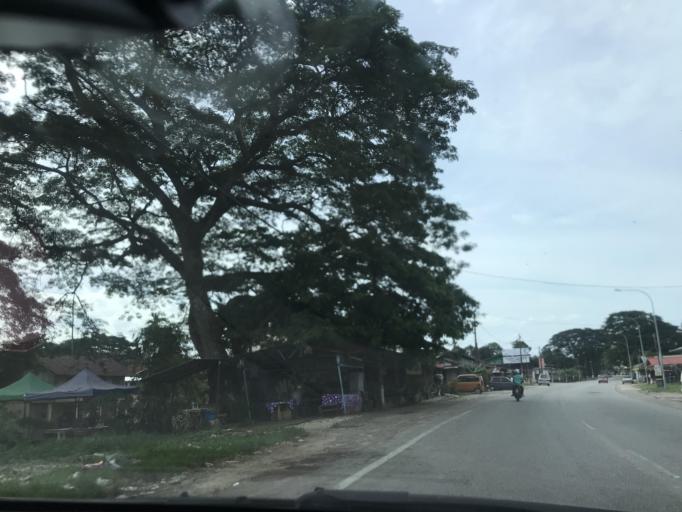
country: MY
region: Kelantan
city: Kota Bharu
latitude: 6.1041
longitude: 102.2354
